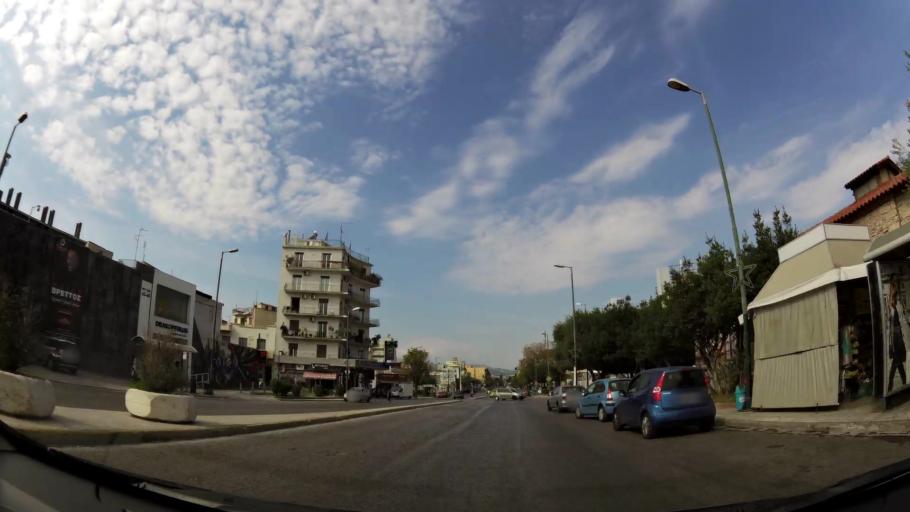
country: GR
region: Attica
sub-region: Nomarchia Athinas
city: Athens
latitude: 37.9805
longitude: 23.7128
